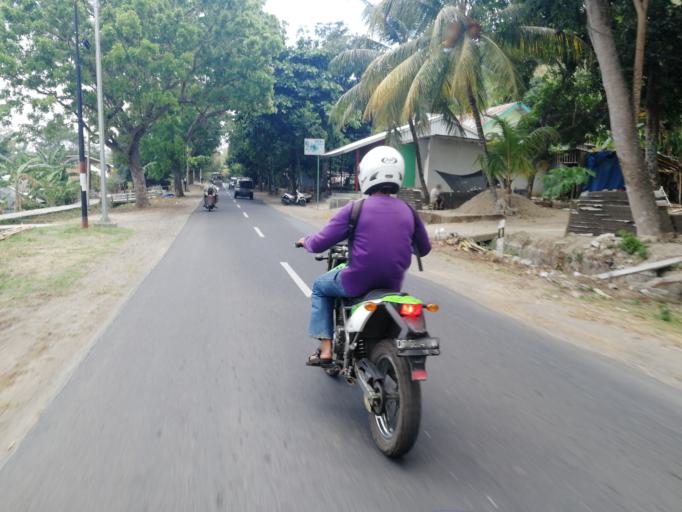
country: ID
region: West Nusa Tenggara
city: Karangsubagan
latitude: -8.4181
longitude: 116.0963
